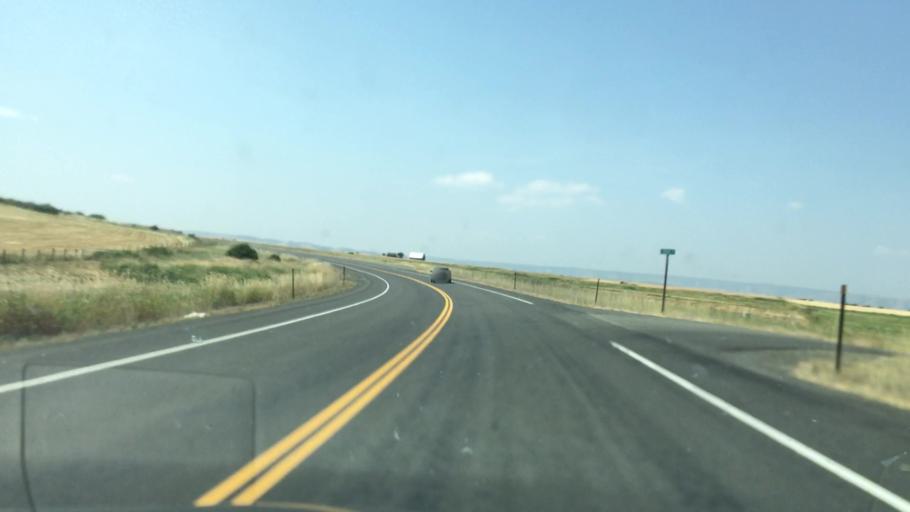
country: US
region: Idaho
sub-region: Idaho County
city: Grangeville
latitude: 45.9250
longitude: -116.1493
